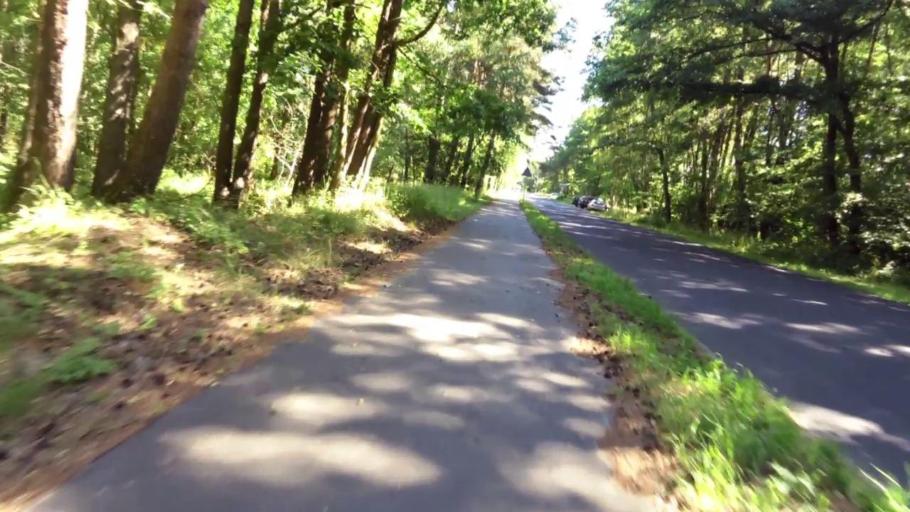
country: PL
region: West Pomeranian Voivodeship
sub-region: Koszalin
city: Koszalin
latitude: 54.3007
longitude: 16.1839
